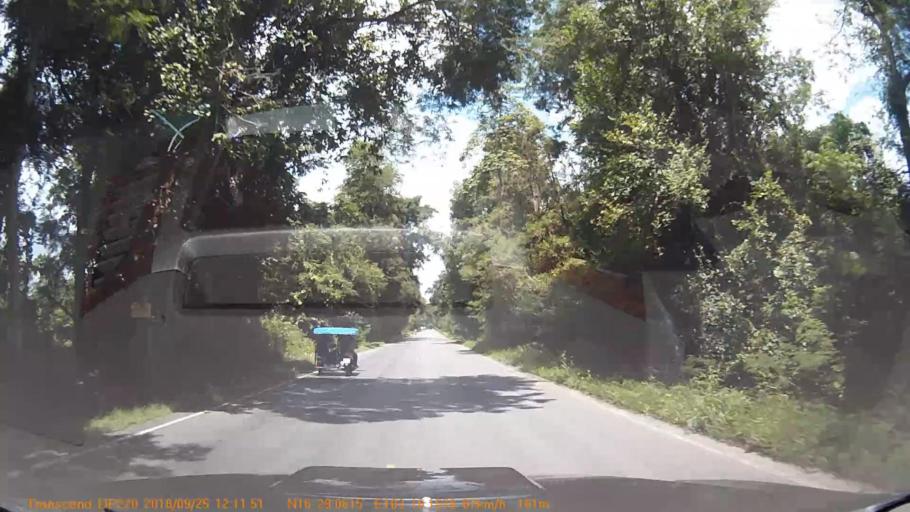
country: TH
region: Kalasin
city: Huai Mek
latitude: 16.4847
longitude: 103.2694
